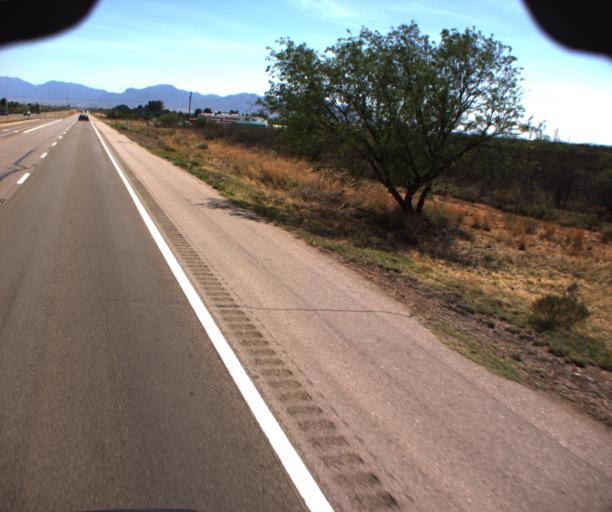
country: US
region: Arizona
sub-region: Cochise County
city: Huachuca City
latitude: 31.7141
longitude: -110.3504
